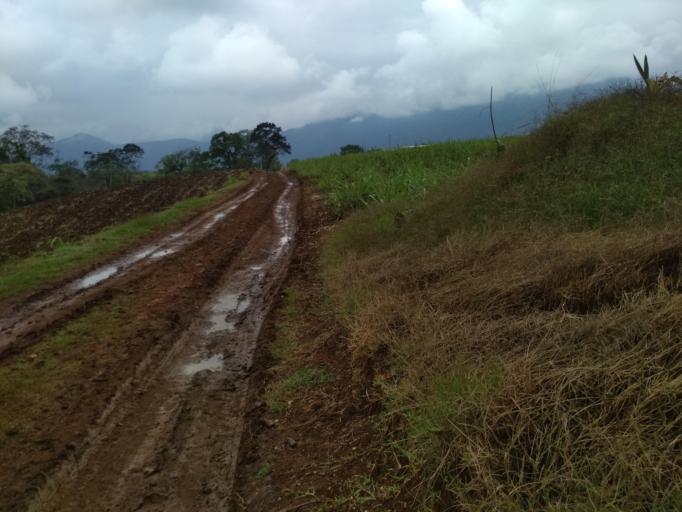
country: MX
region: Veracruz
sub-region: Cordoba
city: San Jose de Tapia
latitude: 18.8500
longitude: -96.9623
